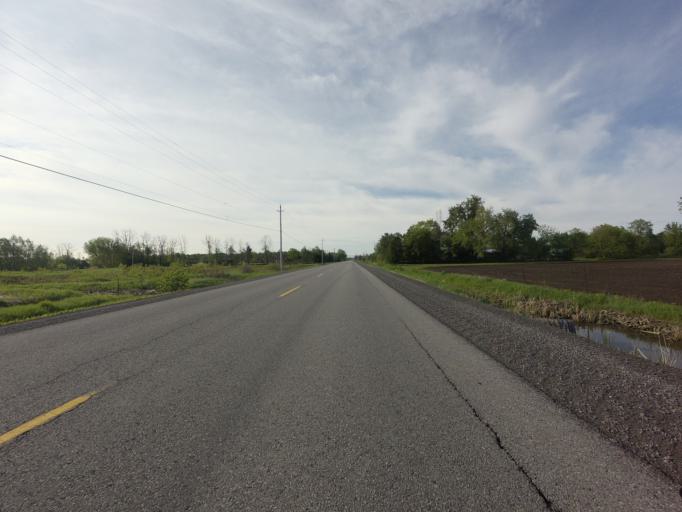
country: CA
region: Ontario
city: Ottawa
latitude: 45.2953
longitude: -75.4510
